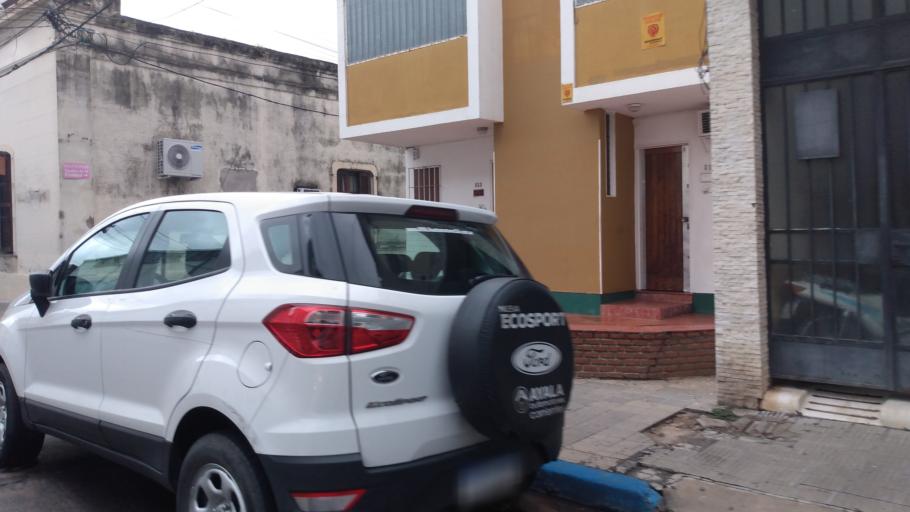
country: AR
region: Corrientes
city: Corrientes
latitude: -27.4641
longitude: -58.8326
